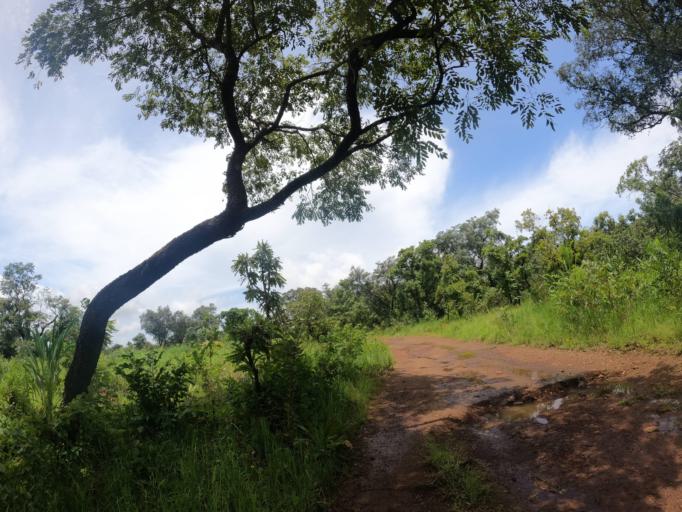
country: SL
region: Northern Province
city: Binkolo
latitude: 9.1563
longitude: -12.2000
